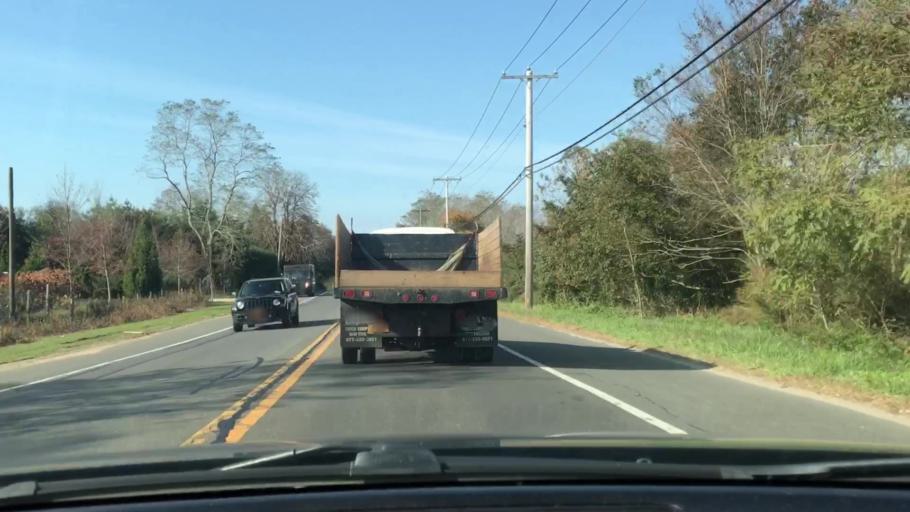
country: US
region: New York
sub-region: Suffolk County
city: Bridgehampton
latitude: 40.9410
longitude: -72.2825
